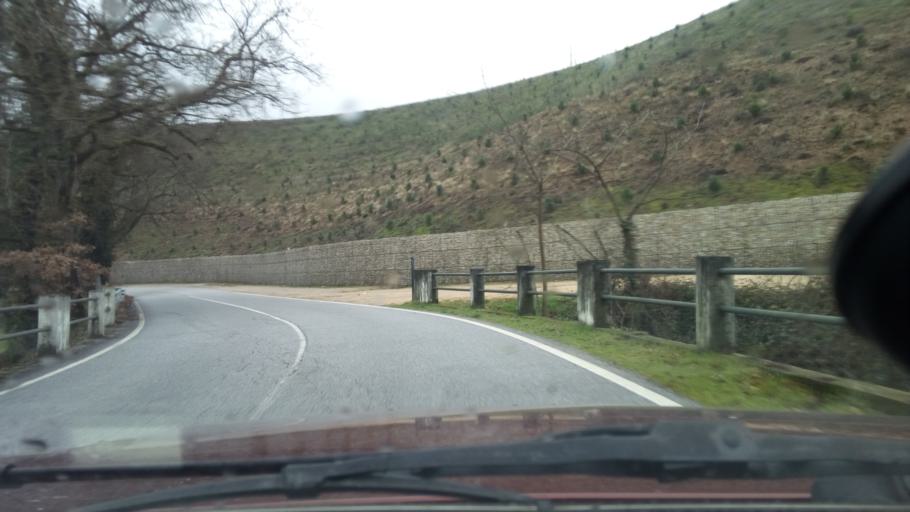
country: PT
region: Viseu
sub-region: Viseu
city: Rio de Loba
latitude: 40.6371
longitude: -7.8324
